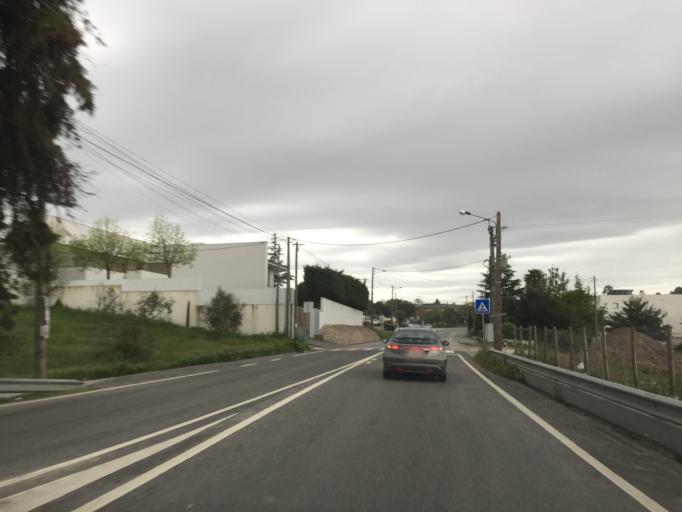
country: PT
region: Leiria
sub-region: Leiria
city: Santa Catarina da Serra
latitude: 39.6723
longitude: -8.6780
